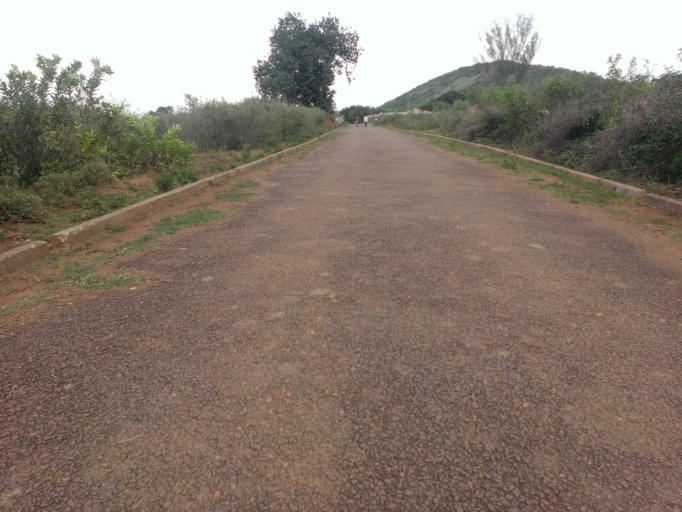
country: UG
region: Eastern Region
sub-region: Busia District
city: Busia
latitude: 0.5436
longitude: 34.0236
